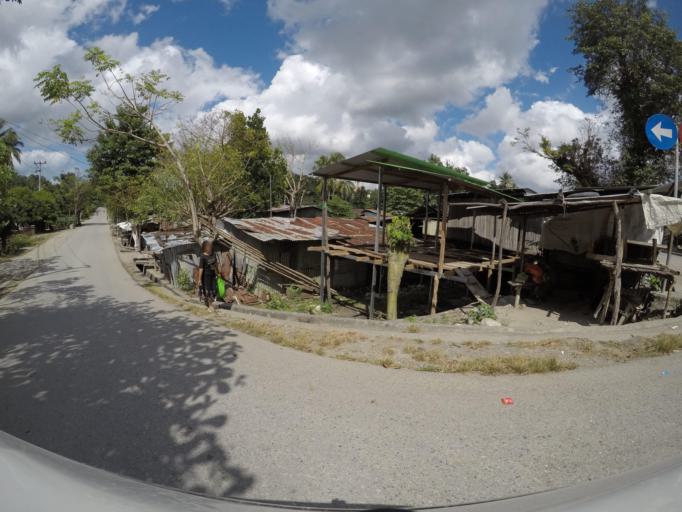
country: TL
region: Viqueque
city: Viqueque
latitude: -8.8676
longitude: 126.3678
